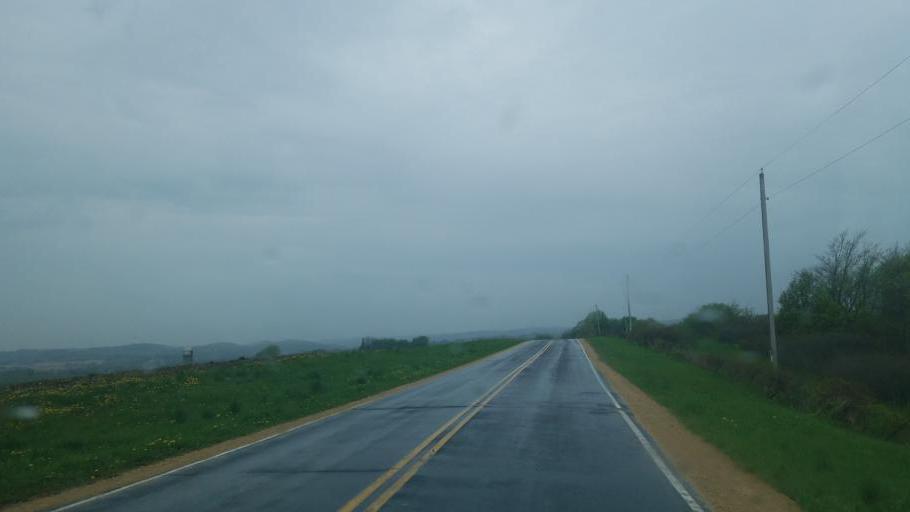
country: US
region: Wisconsin
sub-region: Vernon County
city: Hillsboro
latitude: 43.6509
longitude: -90.3178
